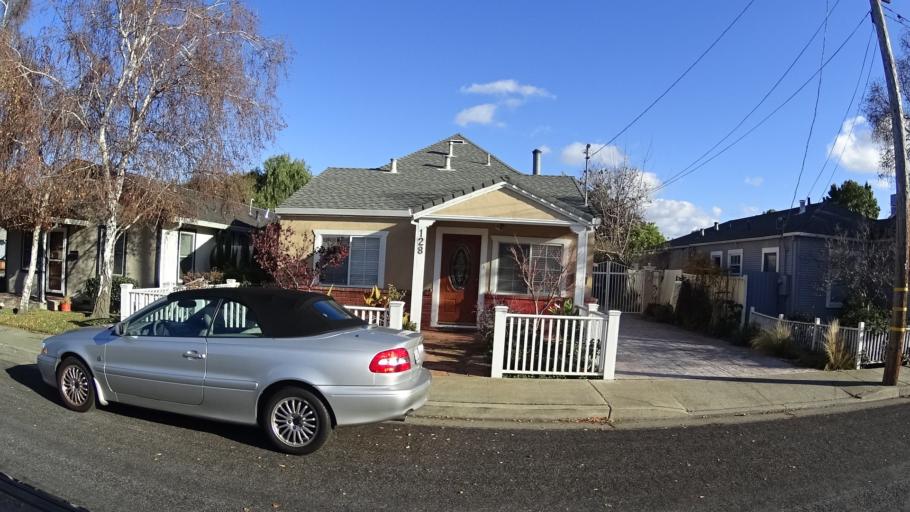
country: US
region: California
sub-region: Santa Clara County
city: Sunnyvale
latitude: 37.3808
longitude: -122.0416
